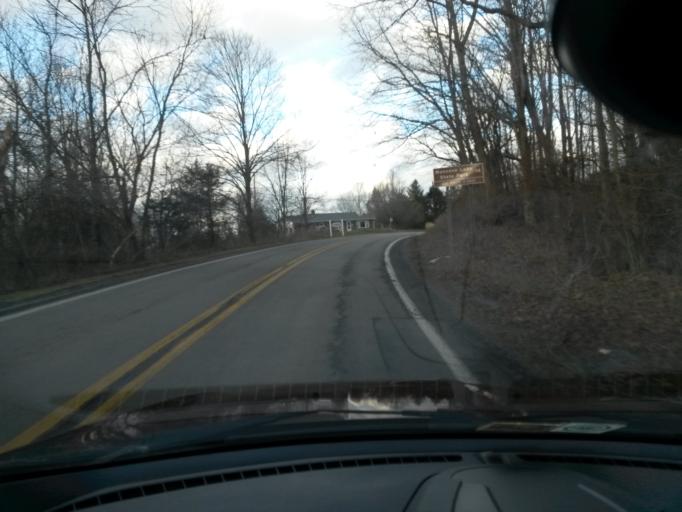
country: US
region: West Virginia
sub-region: Monroe County
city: Union
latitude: 37.5880
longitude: -80.5493
